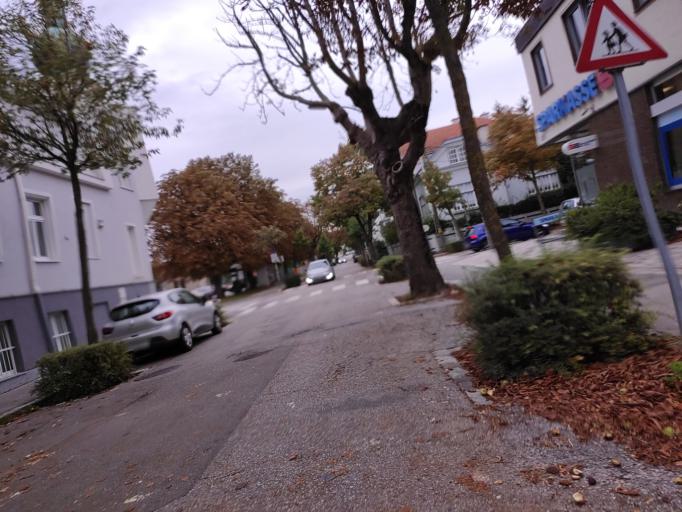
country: AT
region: Lower Austria
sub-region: Politischer Bezirk Baden
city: Baden
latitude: 48.0029
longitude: 16.2177
